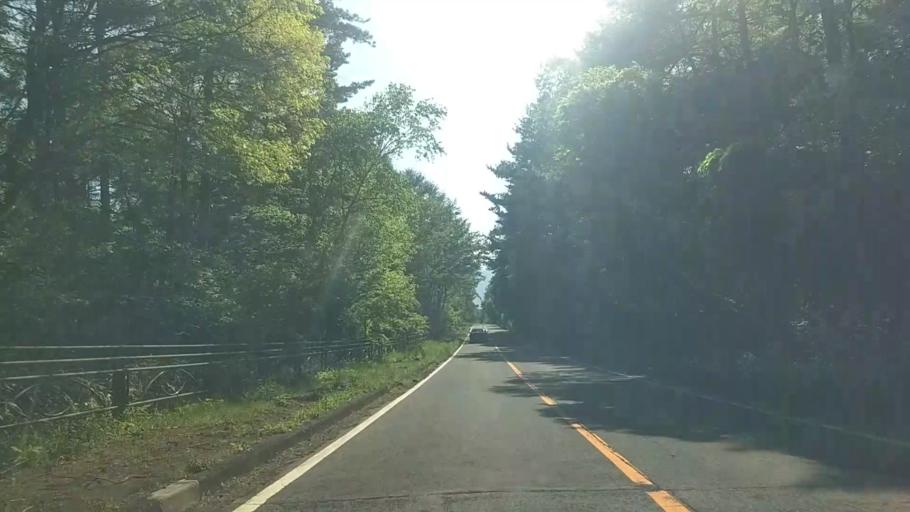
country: JP
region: Nagano
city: Chino
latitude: 35.8988
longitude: 138.3346
